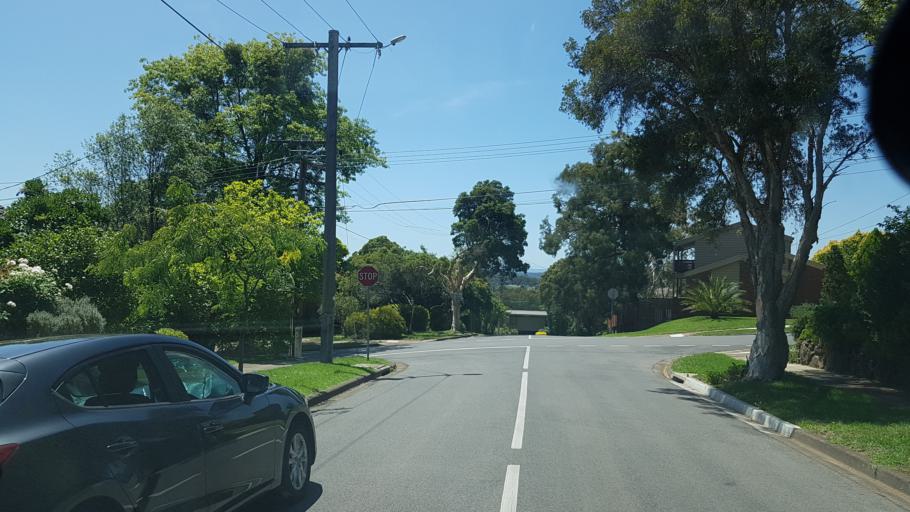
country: AU
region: Victoria
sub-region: Banyule
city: Darch
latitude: -37.7582
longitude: 145.1028
